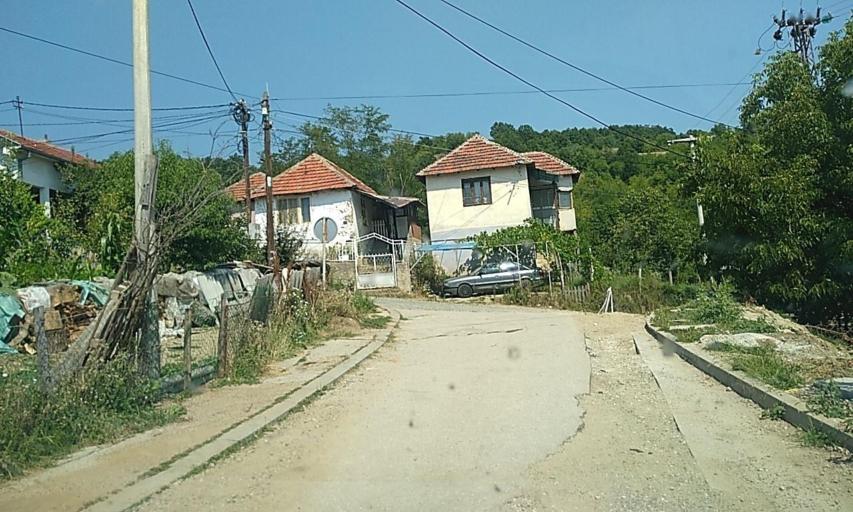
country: RS
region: Central Serbia
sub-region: Pcinjski Okrug
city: Vladicin Han
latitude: 42.7073
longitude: 22.0519
